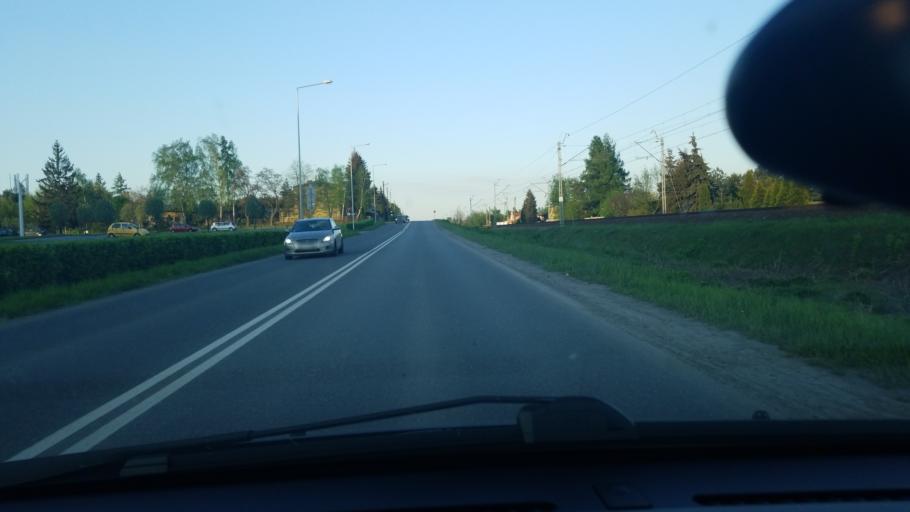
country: PL
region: Silesian Voivodeship
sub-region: Czestochowa
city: Czestochowa
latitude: 50.7969
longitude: 19.0541
